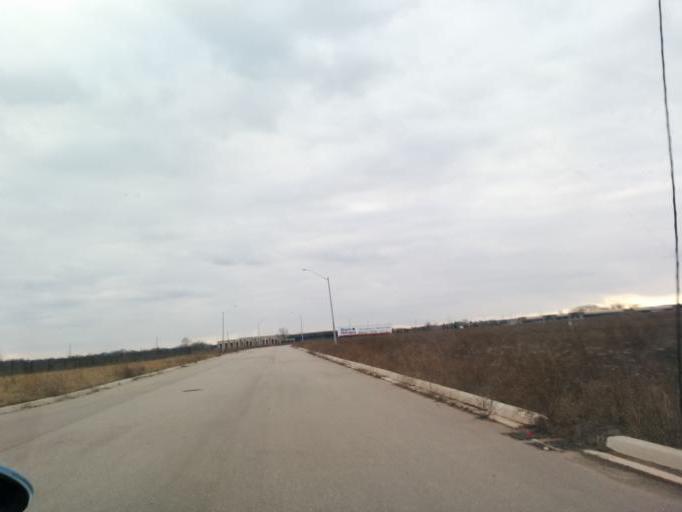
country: CA
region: Ontario
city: Oakville
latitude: 43.3891
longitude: -79.7350
